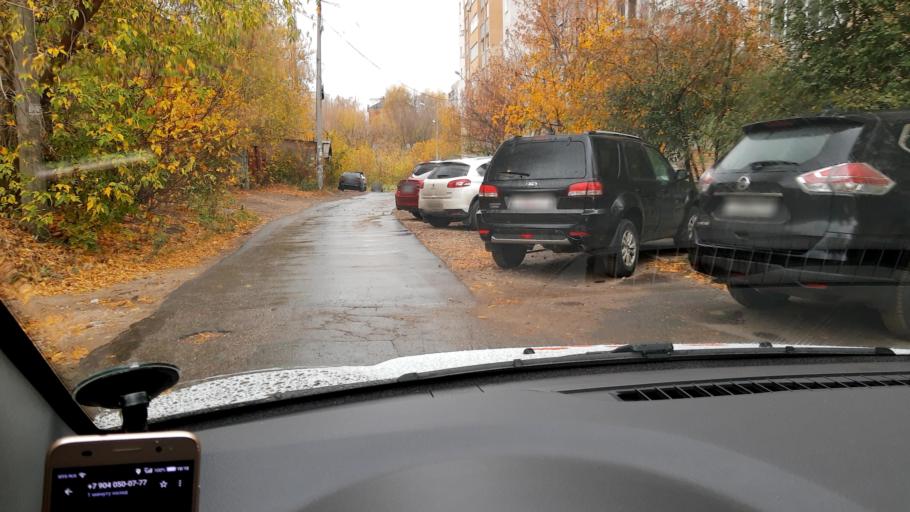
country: RU
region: Nizjnij Novgorod
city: Nizhniy Novgorod
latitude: 56.2947
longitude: 43.9896
